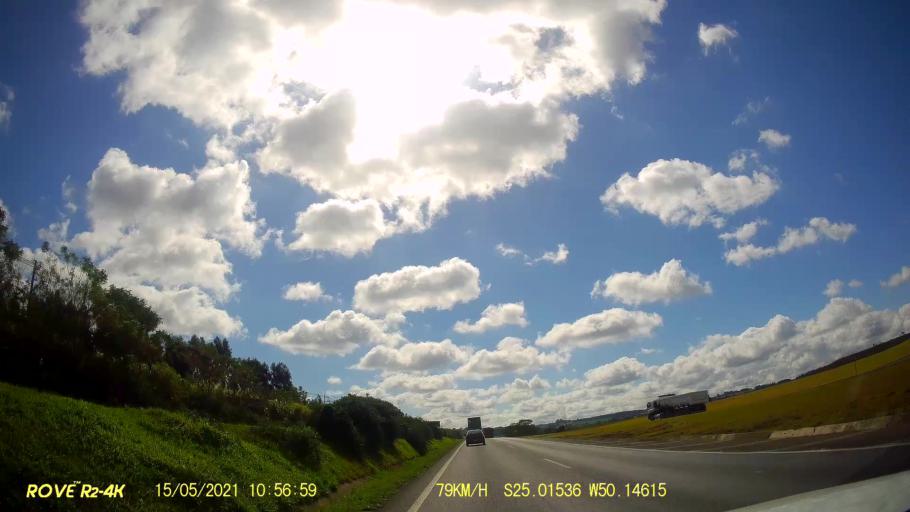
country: BR
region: Parana
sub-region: Carambei
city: Carambei
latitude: -25.0156
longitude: -50.1464
